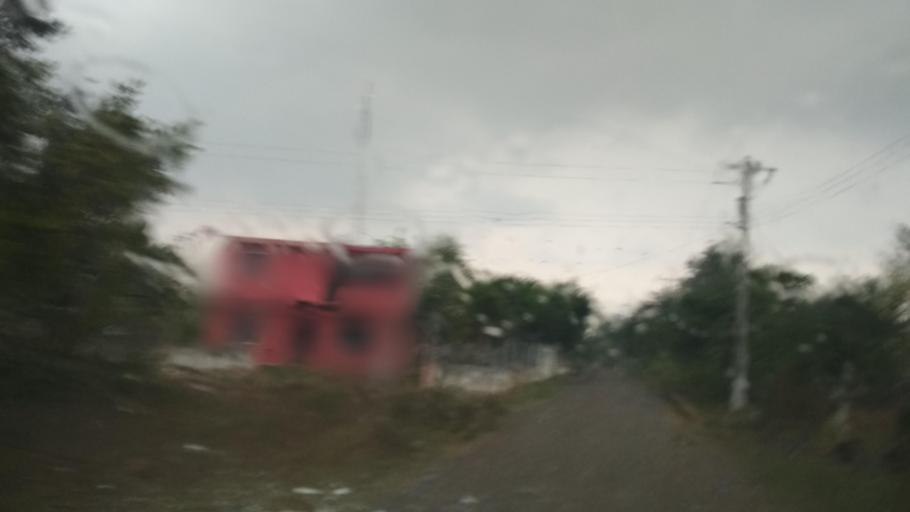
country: MM
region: Shan
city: Taunggyi
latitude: 20.3013
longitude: 97.3065
